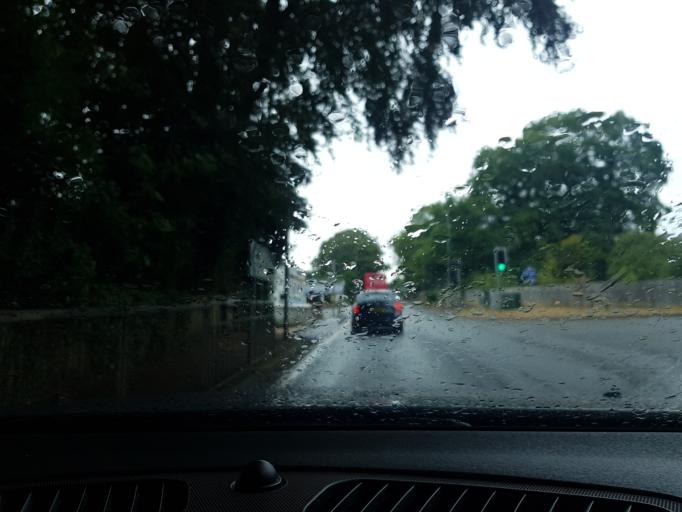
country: GB
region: England
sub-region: Surrey
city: Hale
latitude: 51.2346
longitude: -0.8010
